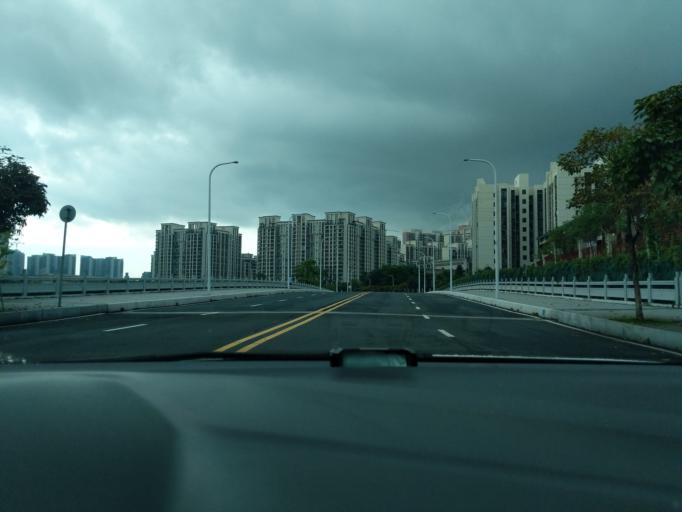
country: CN
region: Guangdong
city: Huangge
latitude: 22.7990
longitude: 113.5172
